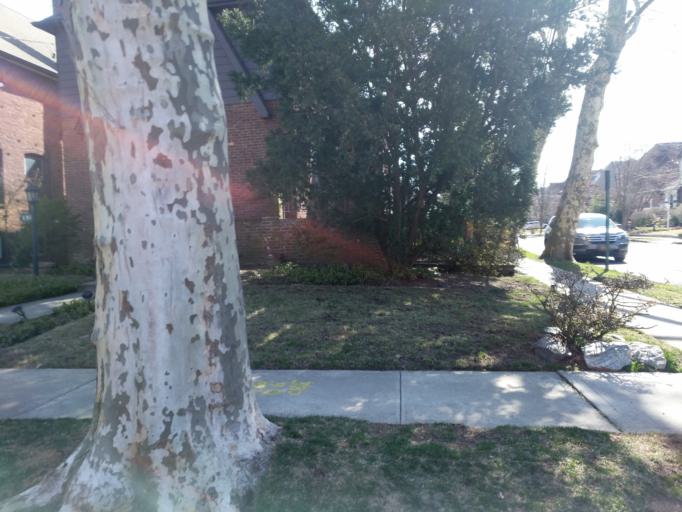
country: US
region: New York
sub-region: Nassau County
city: Hewlett
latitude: 40.6540
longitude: -73.6885
